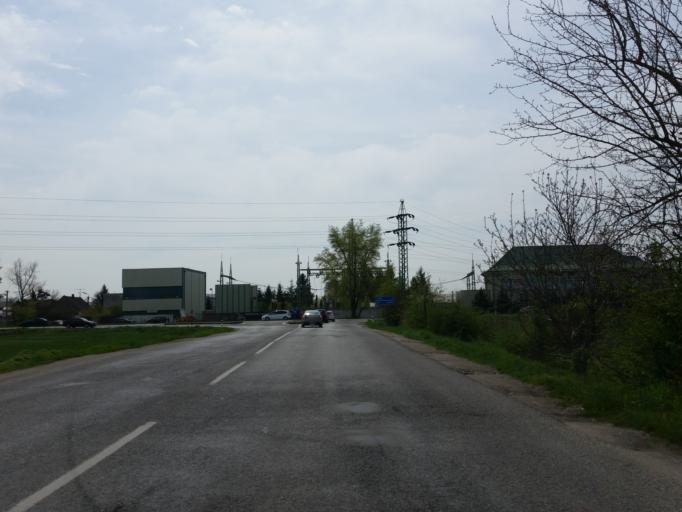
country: SK
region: Trnavsky
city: Leopoldov
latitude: 48.4365
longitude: 17.7676
